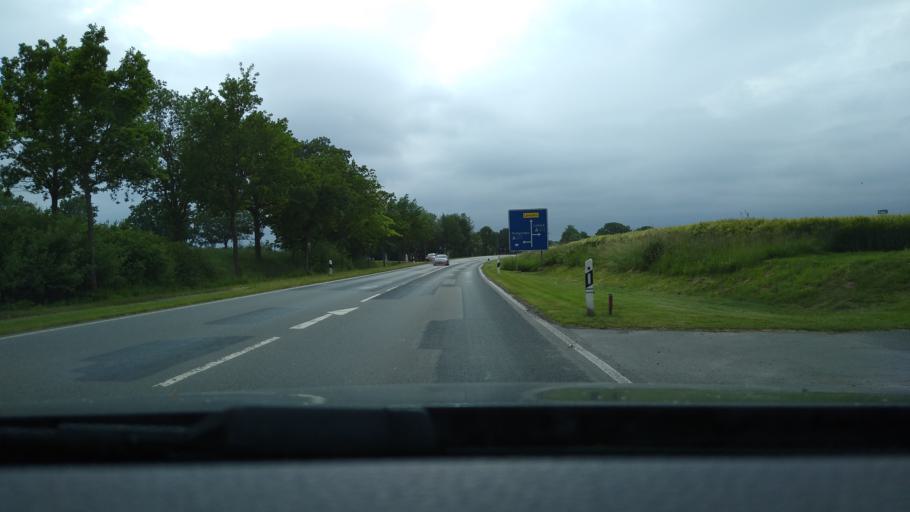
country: DE
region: Schleswig-Holstein
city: Kabelhorst
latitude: 54.2163
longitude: 10.9090
